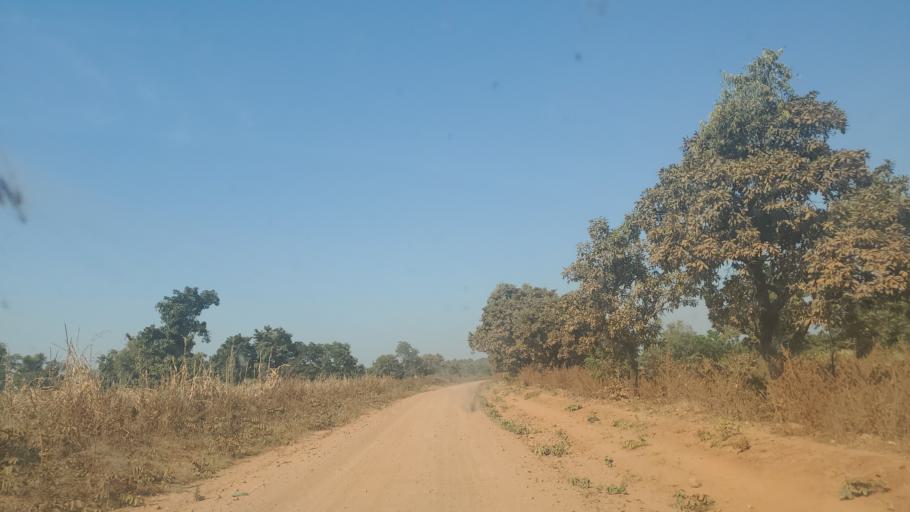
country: NG
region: Niger
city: Badeggi
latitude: 9.1220
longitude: 6.1929
